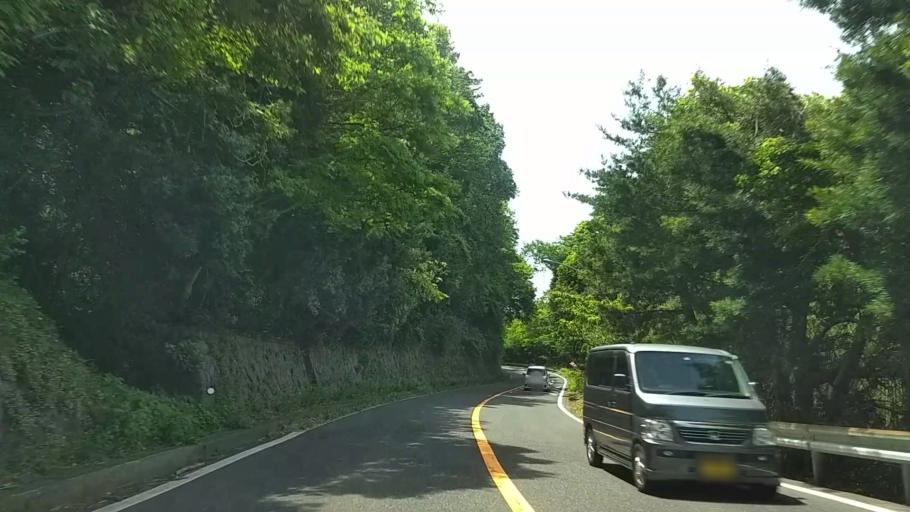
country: JP
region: Kanagawa
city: Yugawara
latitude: 35.1666
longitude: 139.1397
